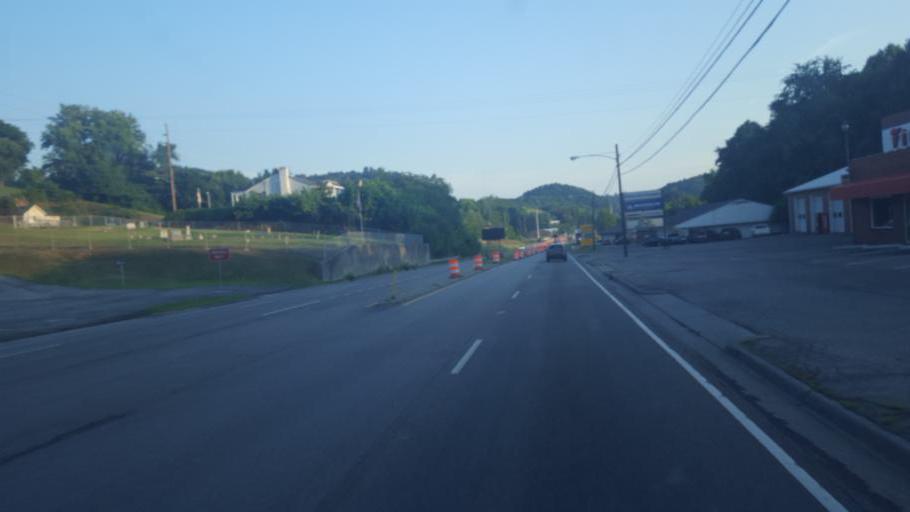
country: US
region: Virginia
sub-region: Scott County
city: Weber City
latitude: 36.6138
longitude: -82.5682
